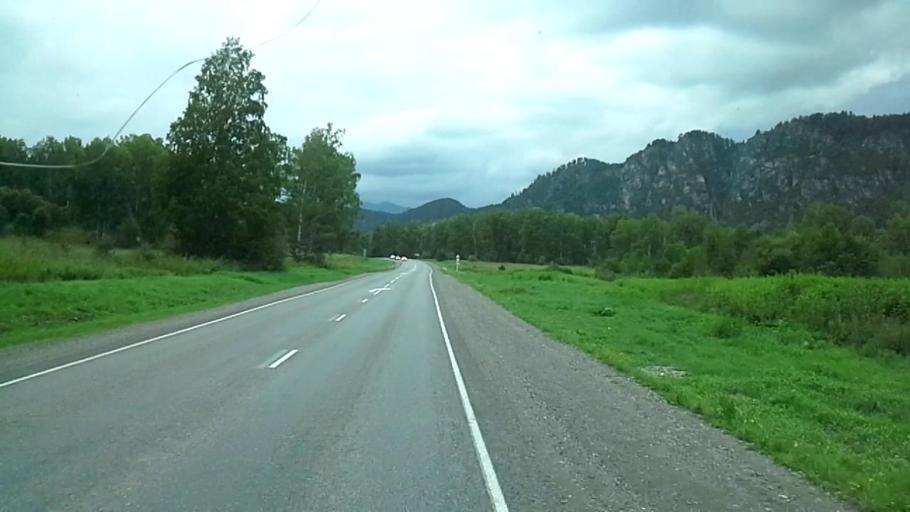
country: RU
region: Altay
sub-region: Mayminskiy Rayon
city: Manzherok
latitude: 51.8560
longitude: 85.7508
